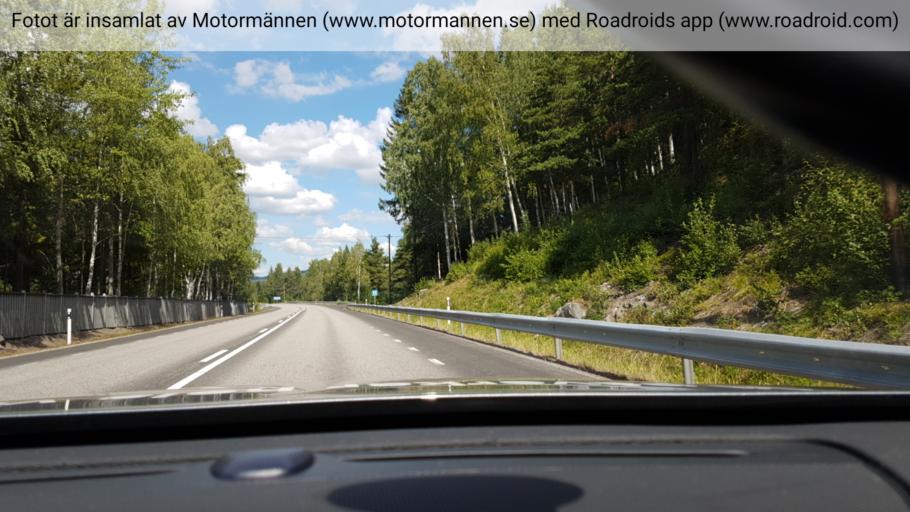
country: SE
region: Dalarna
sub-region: Faluns Kommun
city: Bjursas
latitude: 60.7158
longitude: 15.4596
